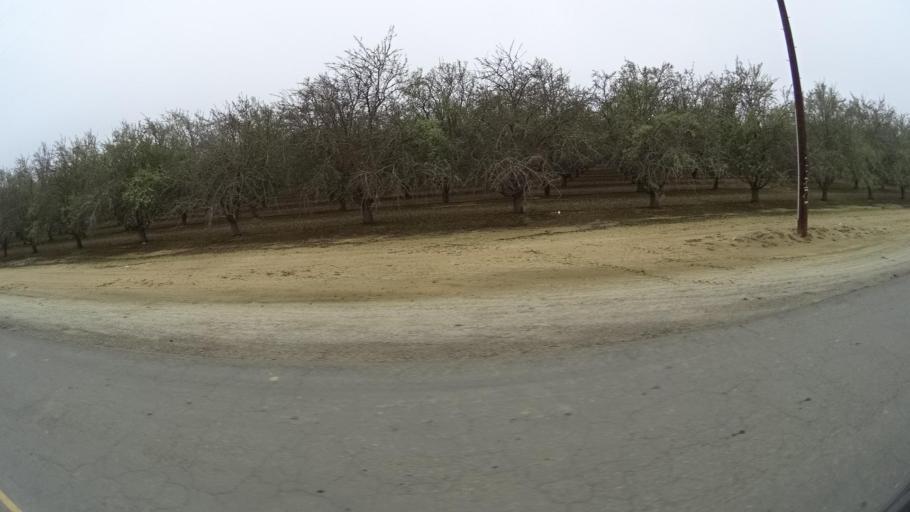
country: US
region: California
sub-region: Kern County
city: Wasco
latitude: 35.5983
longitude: -119.5091
